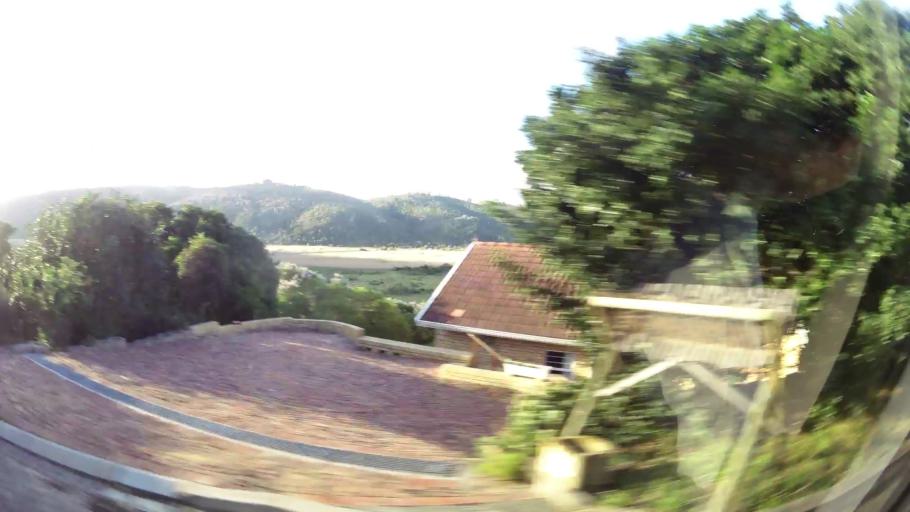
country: ZA
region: Western Cape
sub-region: Eden District Municipality
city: George
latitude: -33.9963
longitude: 22.6201
